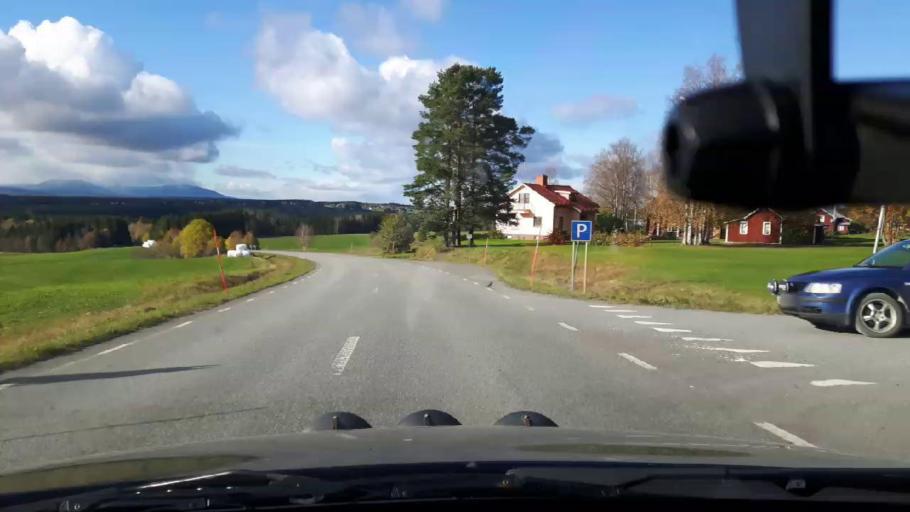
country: SE
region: Jaemtland
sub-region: Bergs Kommun
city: Hoverberg
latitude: 62.9996
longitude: 14.3884
